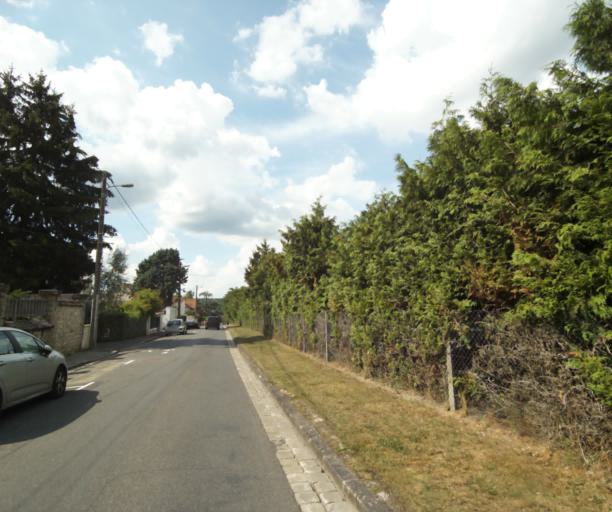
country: FR
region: Ile-de-France
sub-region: Departement de Seine-et-Marne
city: Avon
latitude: 48.4045
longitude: 2.7278
